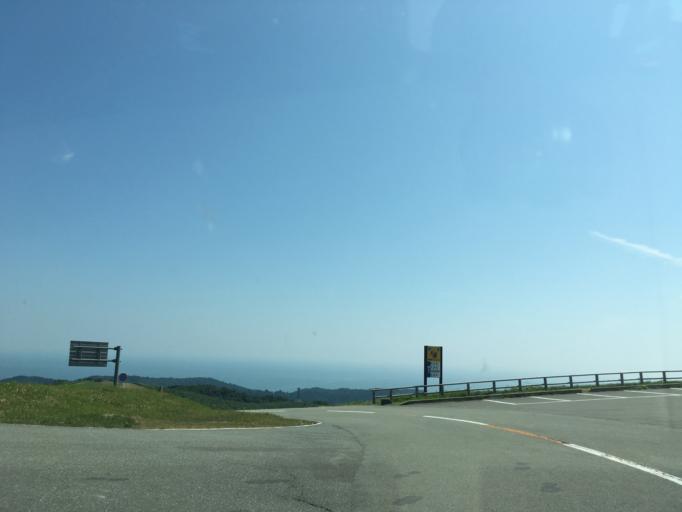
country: JP
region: Akita
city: Tenno
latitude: 39.9310
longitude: 139.8725
